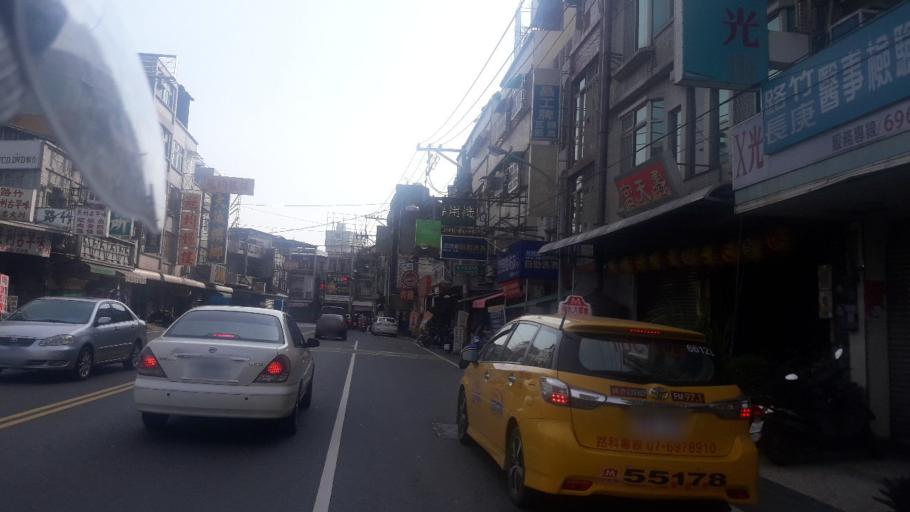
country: TW
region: Taiwan
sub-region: Tainan
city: Tainan
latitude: 22.8609
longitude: 120.2601
